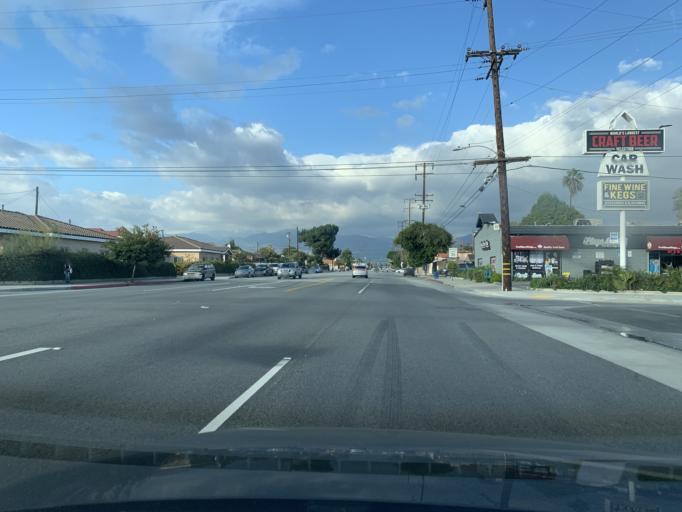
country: US
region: California
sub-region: Los Angeles County
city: El Monte
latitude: 34.0558
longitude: -118.0305
